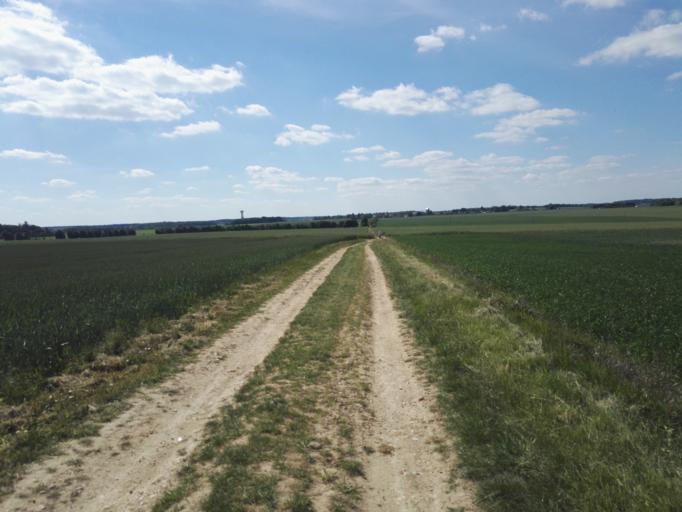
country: FR
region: Haute-Normandie
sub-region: Departement de l'Eure
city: Menilles
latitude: 49.0018
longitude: 1.3296
